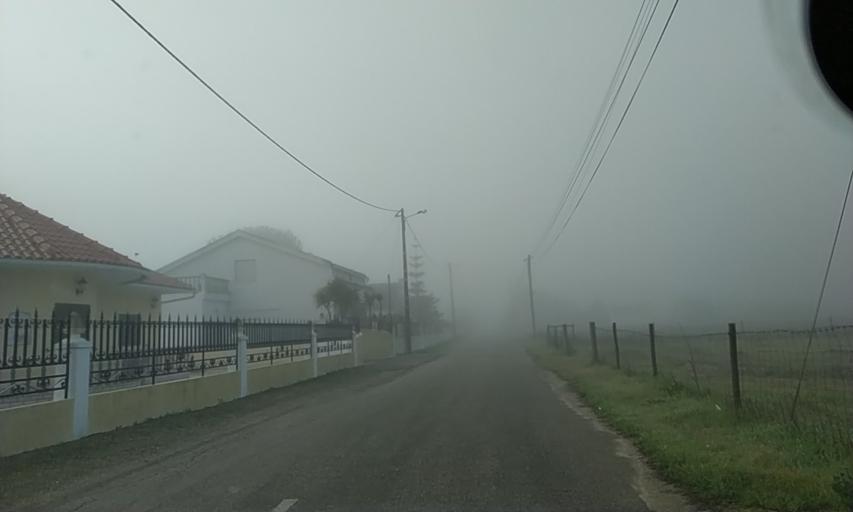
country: PT
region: Setubal
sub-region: Palmela
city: Pinhal Novo
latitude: 38.6104
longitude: -8.8830
